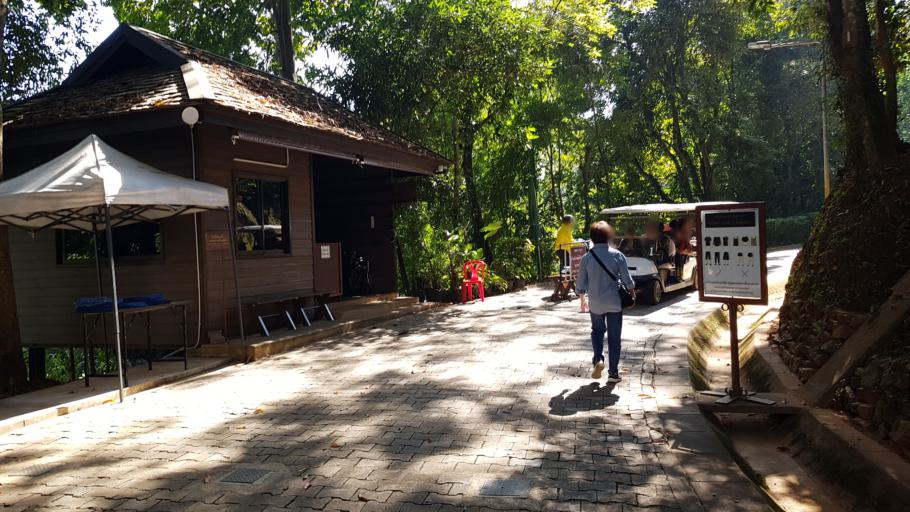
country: TH
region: Chiang Rai
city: Mae Fa Luang
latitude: 20.2880
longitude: 99.8110
